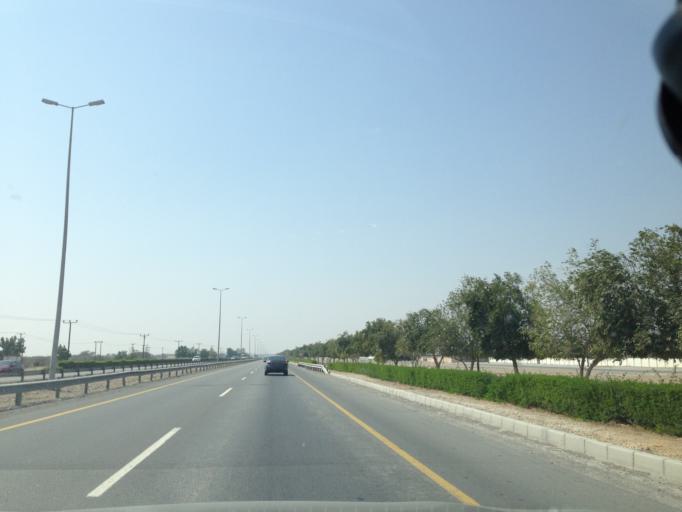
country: OM
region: Al Batinah
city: Barka'
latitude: 23.6685
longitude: 57.9669
